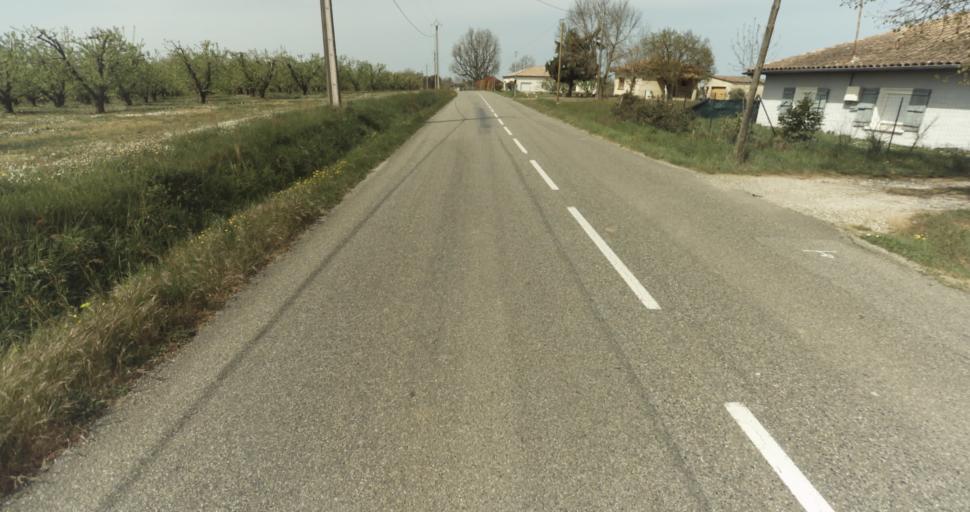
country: FR
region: Midi-Pyrenees
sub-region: Departement du Tarn-et-Garonne
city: Moissac
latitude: 44.1645
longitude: 1.0907
